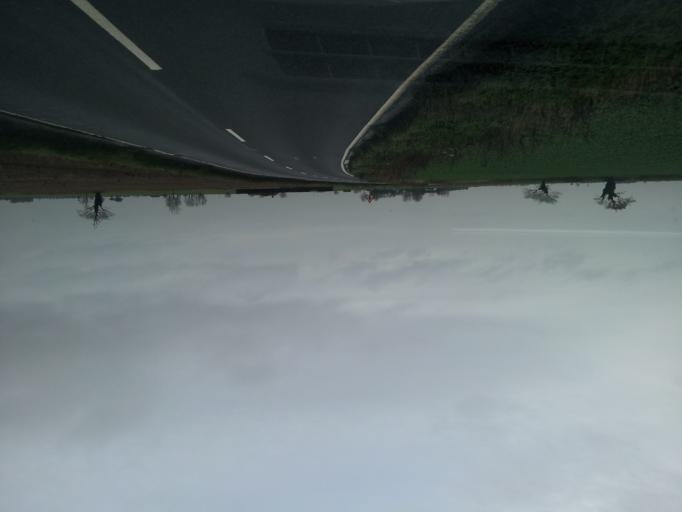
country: GB
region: England
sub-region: Norfolk
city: Martham
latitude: 52.6772
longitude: 1.5941
